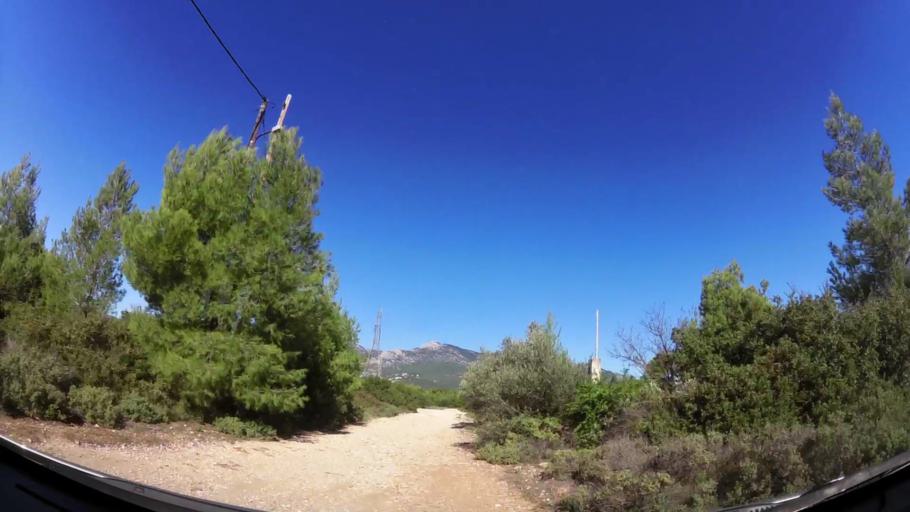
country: GR
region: Attica
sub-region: Nomarchia Anatolikis Attikis
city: Varybobi
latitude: 38.1212
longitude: 23.7805
